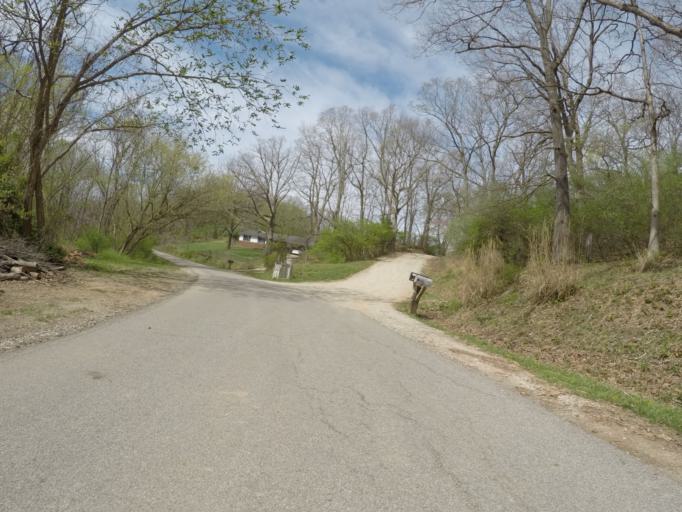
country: US
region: West Virginia
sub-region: Wayne County
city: Lavalette
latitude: 38.3459
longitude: -82.3816
